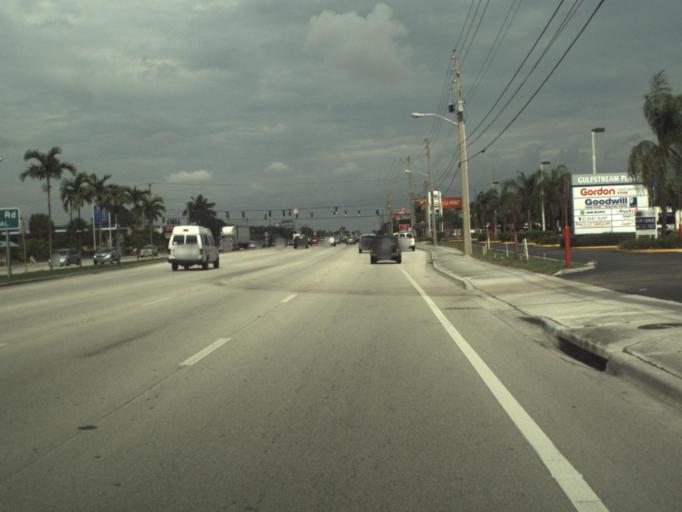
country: US
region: Florida
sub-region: Palm Beach County
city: Schall Circle
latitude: 26.7071
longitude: -80.1172
